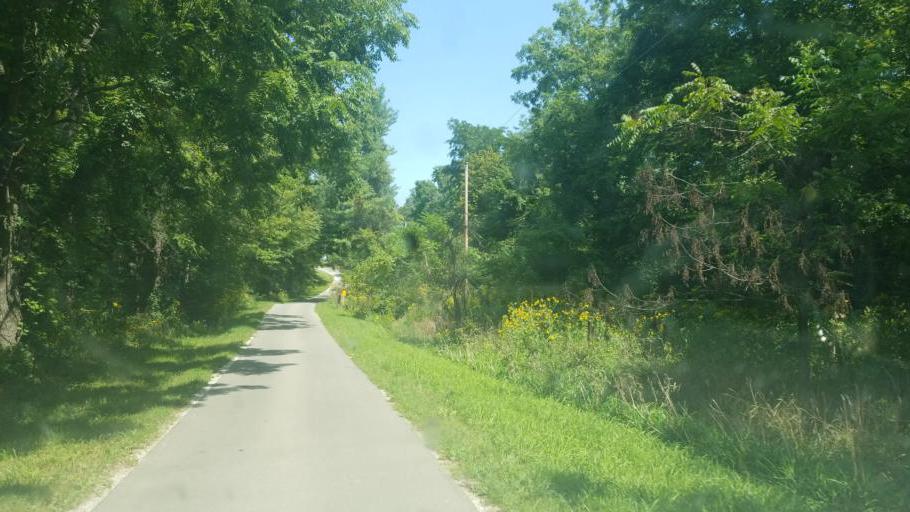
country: US
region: Ohio
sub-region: Crawford County
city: Bucyrus
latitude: 40.9338
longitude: -83.0617
